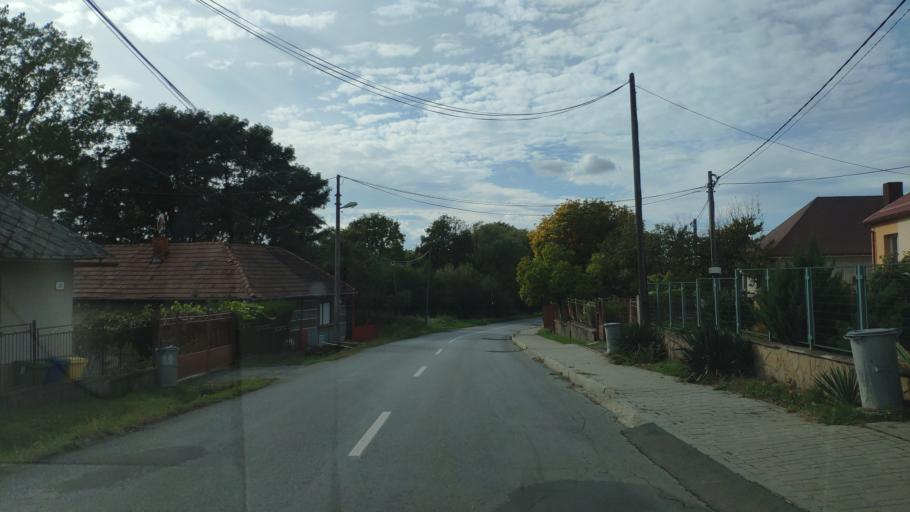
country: SK
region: Presovsky
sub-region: Okres Presov
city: Presov
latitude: 48.9515
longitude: 21.3101
